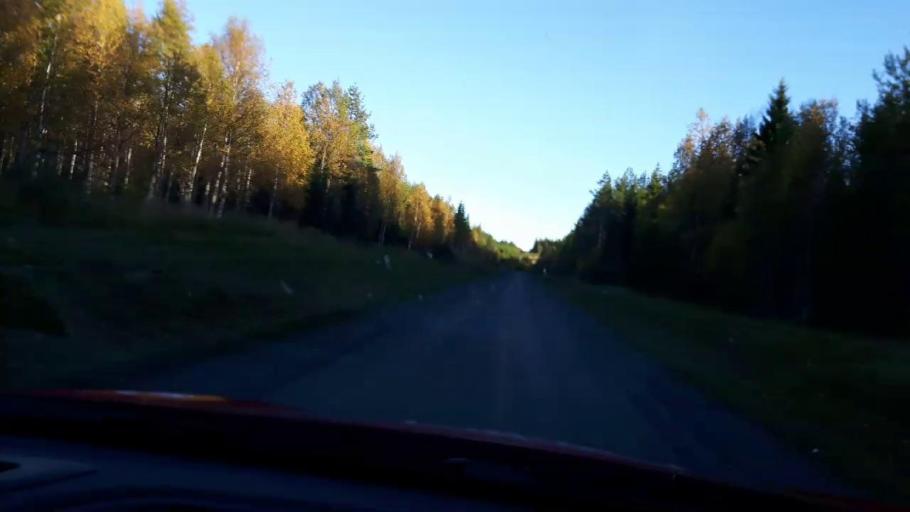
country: SE
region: Jaemtland
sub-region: OEstersunds Kommun
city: Lit
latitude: 63.5889
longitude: 14.8445
